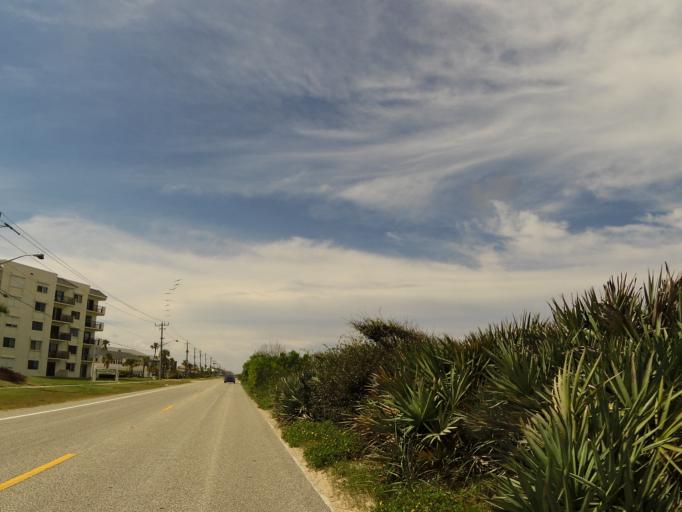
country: US
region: Florida
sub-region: Volusia County
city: Ormond-by-the-Sea
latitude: 29.3634
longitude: -81.0733
